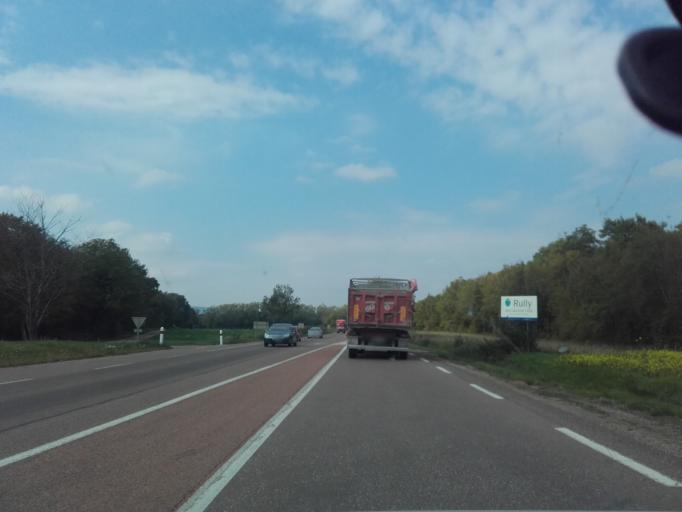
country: FR
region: Bourgogne
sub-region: Departement de Saone-et-Loire
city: Fontaines
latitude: 46.8728
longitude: 4.7881
